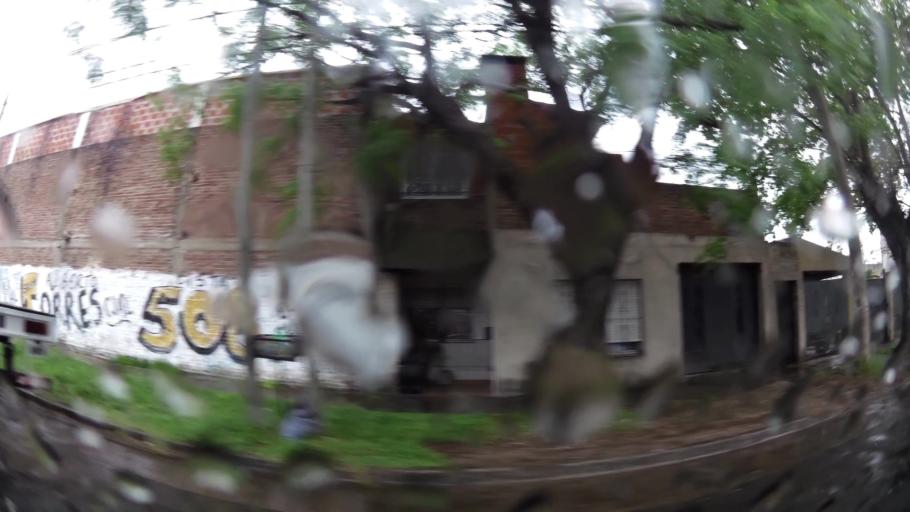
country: AR
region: Buenos Aires
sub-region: Partido de Lanus
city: Lanus
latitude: -34.7060
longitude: -58.4131
